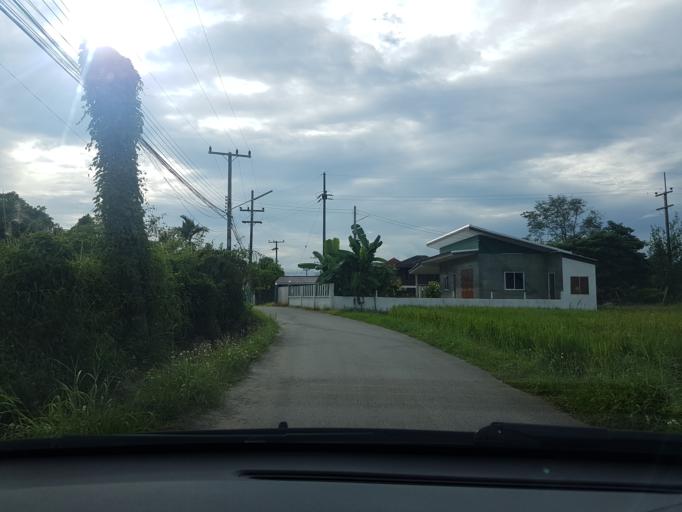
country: TH
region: Chiang Mai
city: San Sai
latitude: 18.8876
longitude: 99.0632
